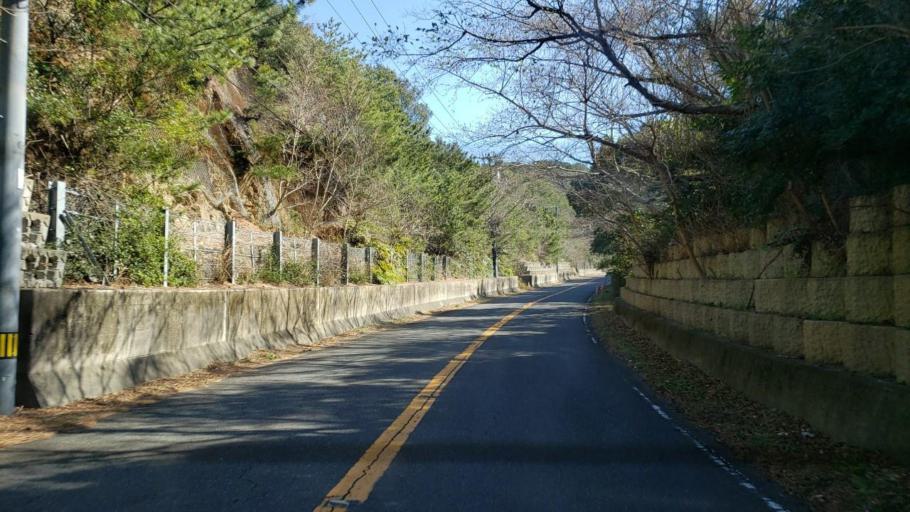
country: JP
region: Tokushima
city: Narutocho-mitsuishi
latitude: 34.2303
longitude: 134.5973
